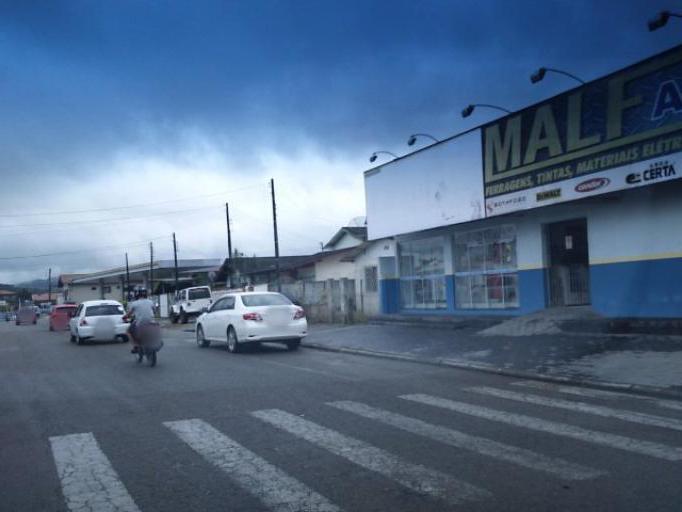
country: BR
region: Santa Catarina
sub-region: Itajai
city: Itajai
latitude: -26.8992
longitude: -48.7010
